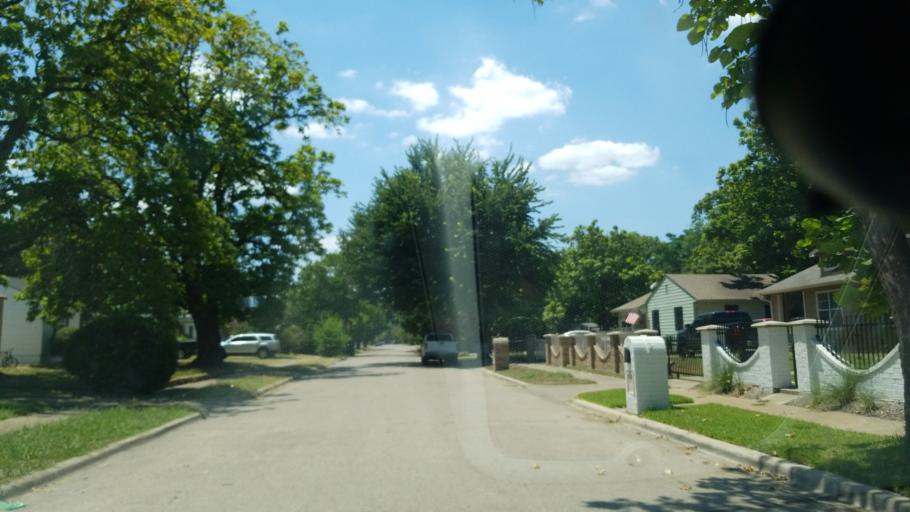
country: US
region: Texas
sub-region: Dallas County
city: Cockrell Hill
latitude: 32.7151
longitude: -96.8514
